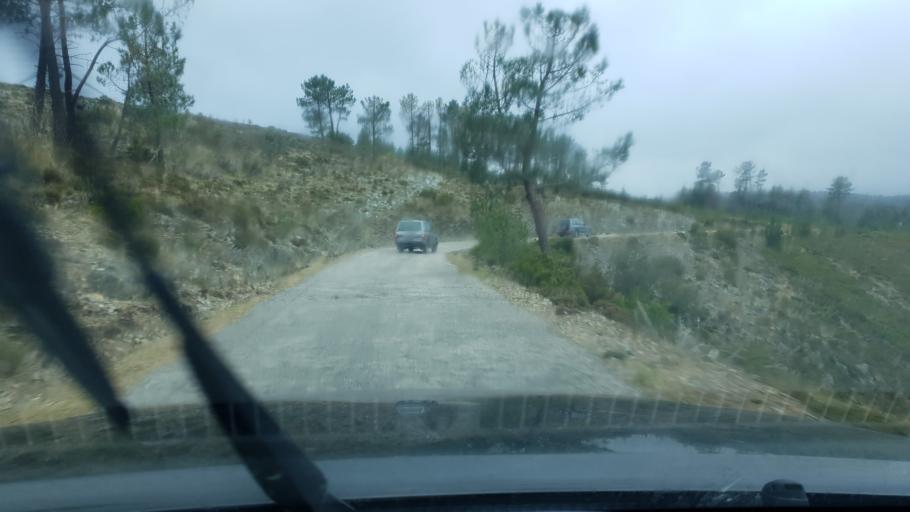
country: PT
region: Viseu
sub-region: Sao Pedro do Sul
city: Sao Pedro do Sul
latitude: 40.8693
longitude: -8.0815
